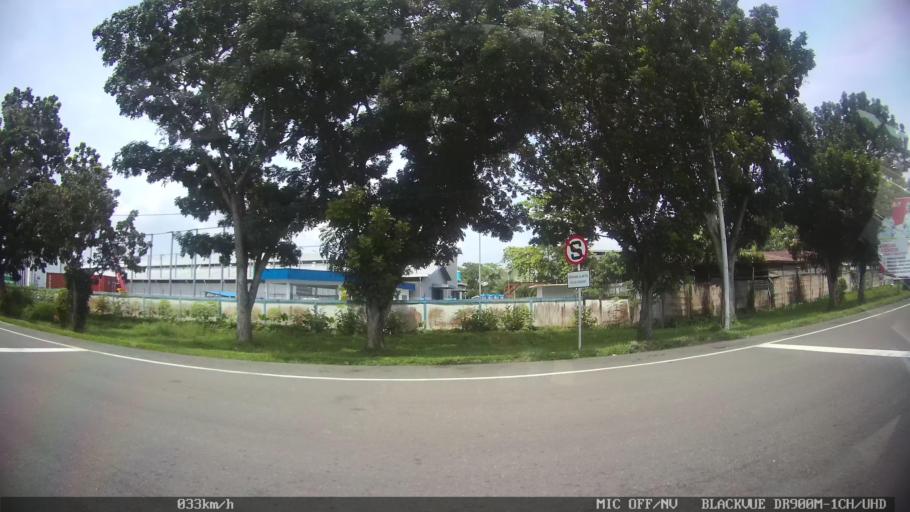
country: ID
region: North Sumatra
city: Labuhan Deli
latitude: 3.7281
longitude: 98.6813
